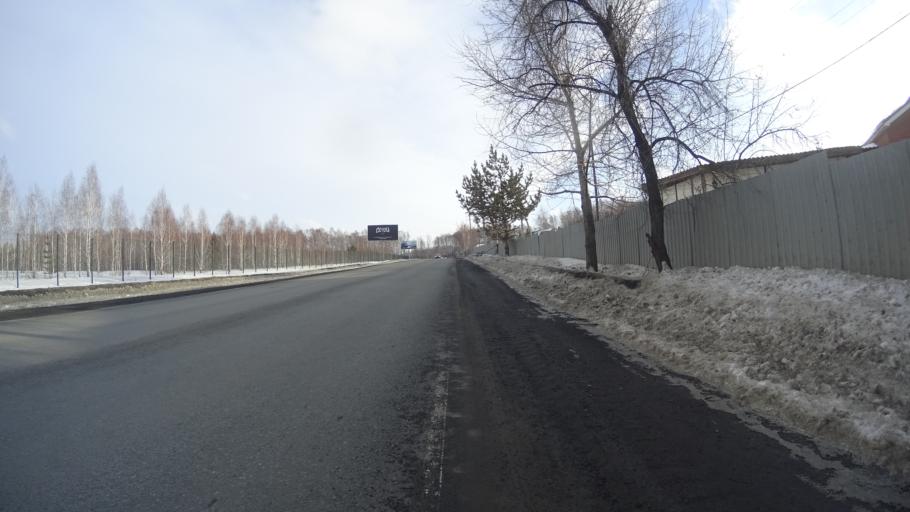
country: RU
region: Chelyabinsk
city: Sargazy
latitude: 55.1314
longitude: 61.2871
